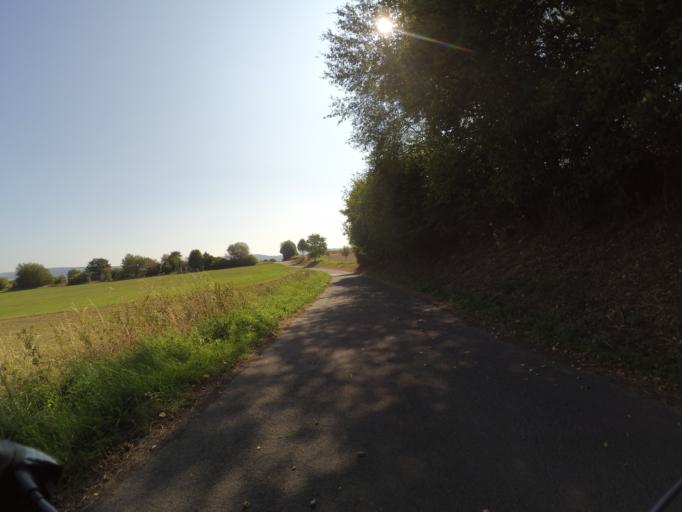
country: DE
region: Rheinland-Pfalz
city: Immert
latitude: 49.7641
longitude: 7.0240
